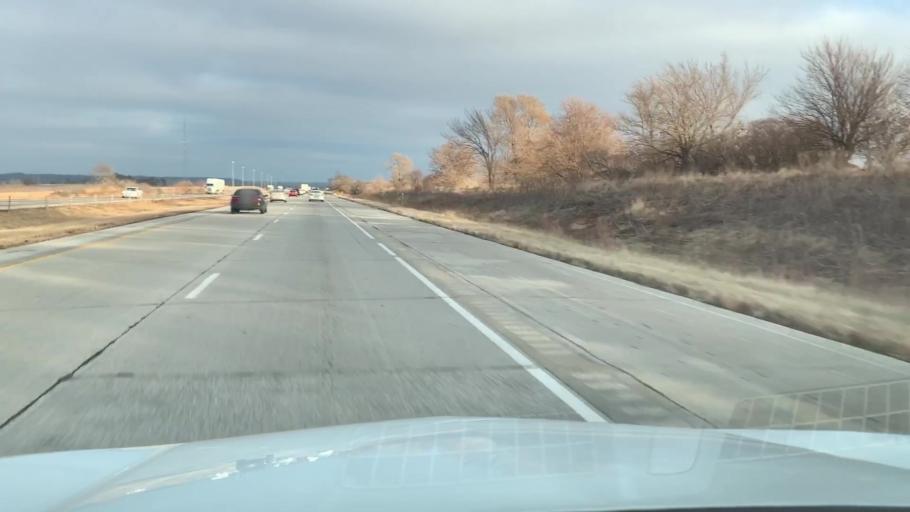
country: US
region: Iowa
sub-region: Polk County
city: Mitchellville
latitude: 41.6806
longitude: -93.3526
